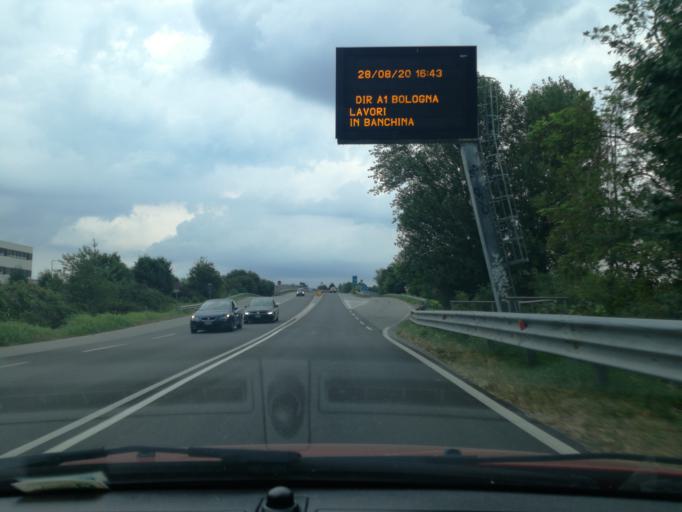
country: IT
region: Lombardy
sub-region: Provincia di Monza e Brianza
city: Usmate-Velate
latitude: 45.6405
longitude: 9.3596
